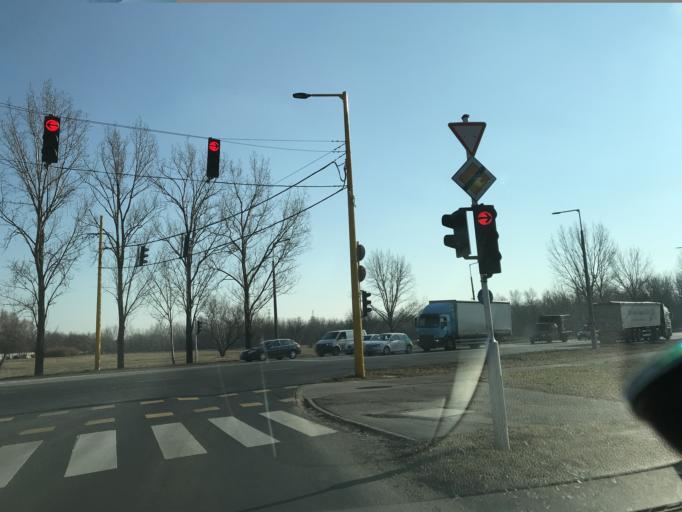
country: HU
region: Gyor-Moson-Sopron
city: Gyor
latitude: 47.6609
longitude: 17.6376
